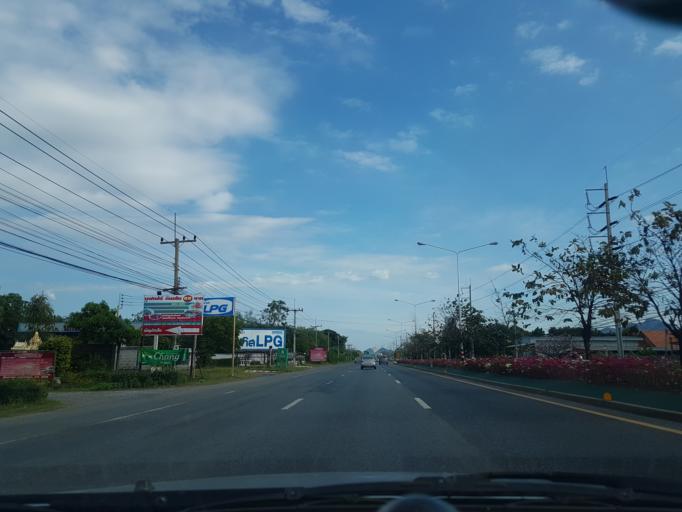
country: TH
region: Sara Buri
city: Phra Phutthabat
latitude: 14.7397
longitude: 100.7676
